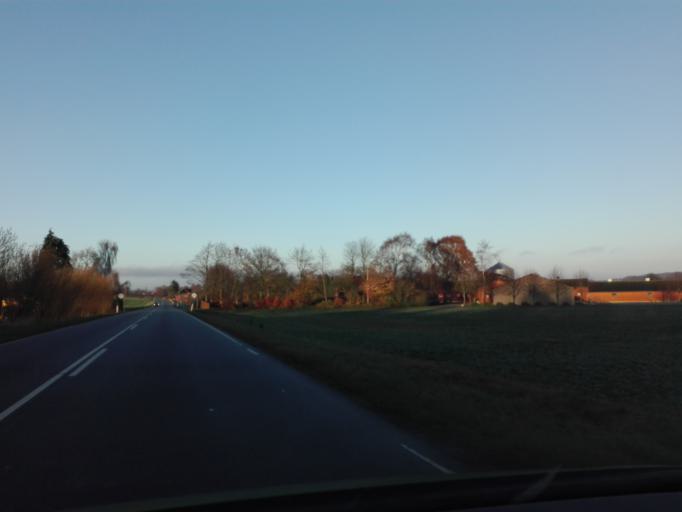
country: DK
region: Central Jutland
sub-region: Skanderborg Kommune
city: Skanderborg
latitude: 56.0884
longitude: 9.8989
